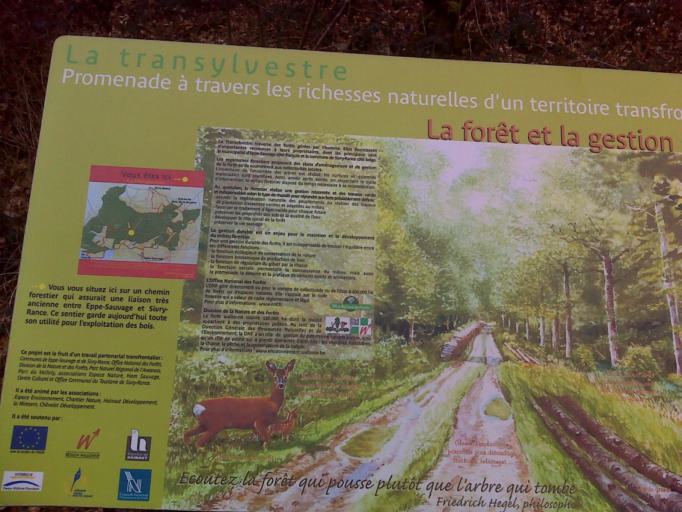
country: FR
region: Nord-Pas-de-Calais
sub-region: Departement du Nord
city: Trelon
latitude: 50.1347
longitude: 4.1659
